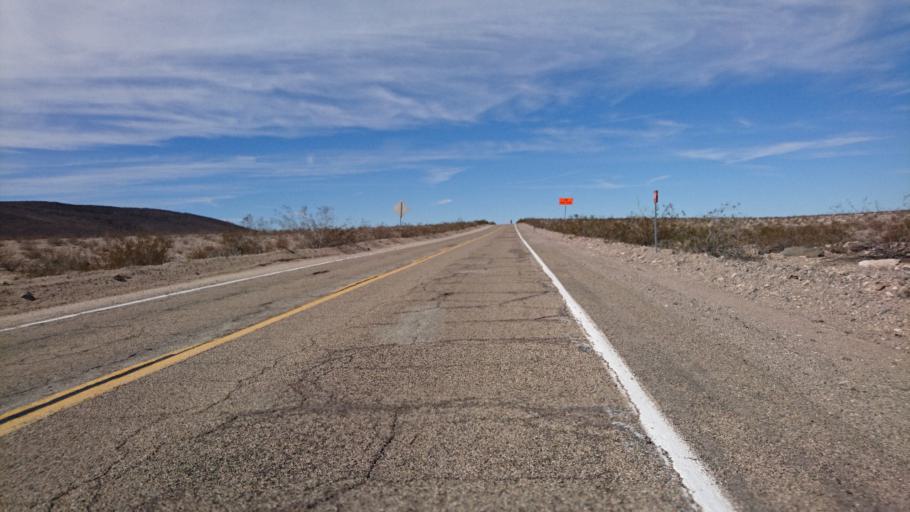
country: US
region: California
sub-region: San Bernardino County
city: Twentynine Palms
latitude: 34.6982
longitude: -116.0599
